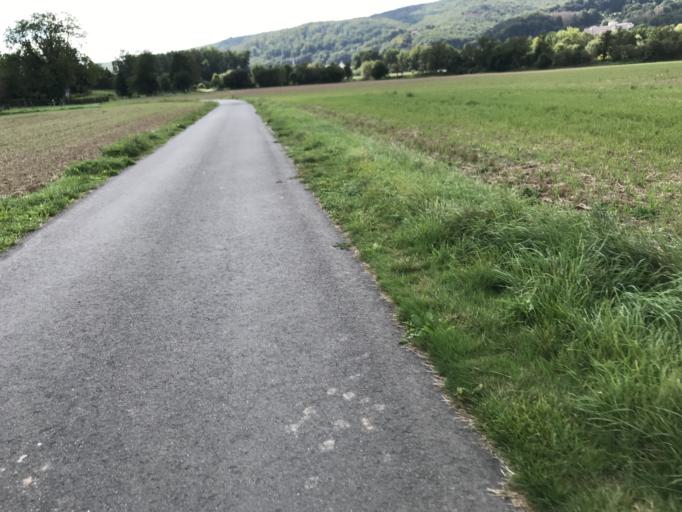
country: DE
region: Hesse
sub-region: Regierungsbezirk Kassel
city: Bad Sooden-Allendorf
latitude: 51.2802
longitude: 9.9678
